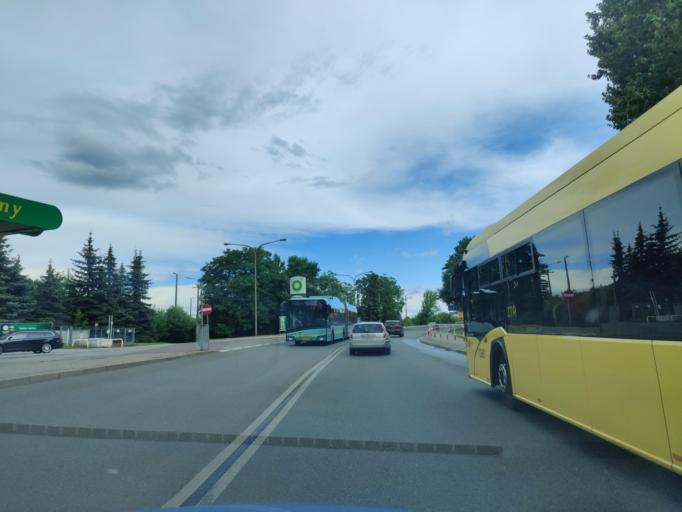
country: PL
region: Silesian Voivodeship
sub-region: Sosnowiec
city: Sosnowiec
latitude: 50.2465
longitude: 19.1292
